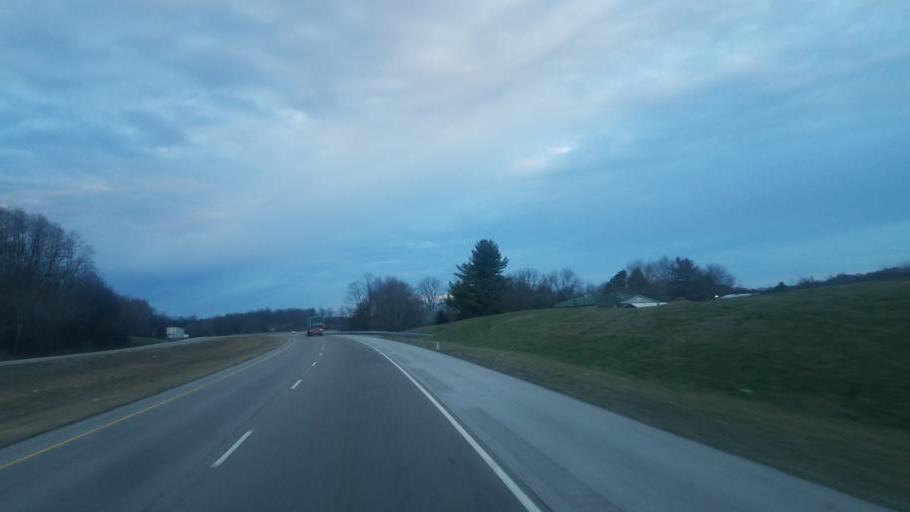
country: US
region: Tennessee
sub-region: White County
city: Sparta
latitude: 35.9788
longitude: -85.4929
